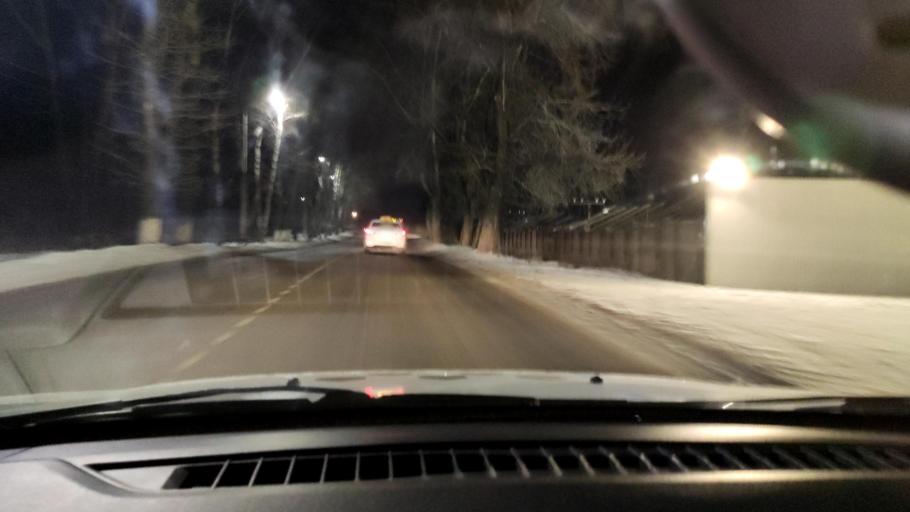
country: RU
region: Perm
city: Kultayevo
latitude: 57.9868
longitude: 55.9236
